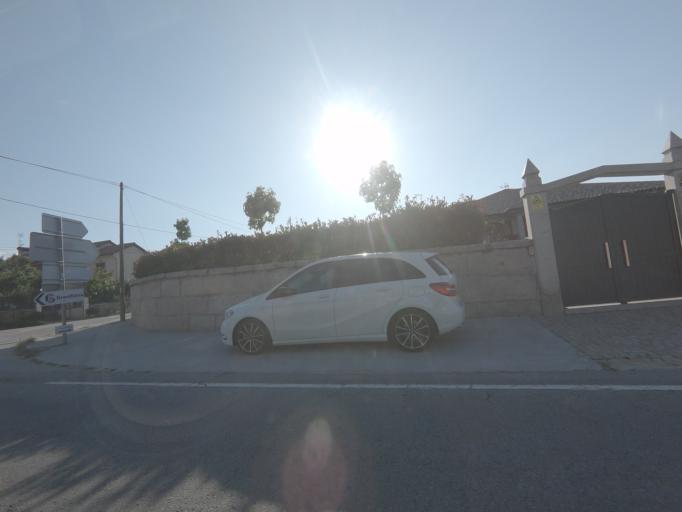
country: PT
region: Vila Real
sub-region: Chaves
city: Chaves
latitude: 41.8026
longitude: -7.4200
